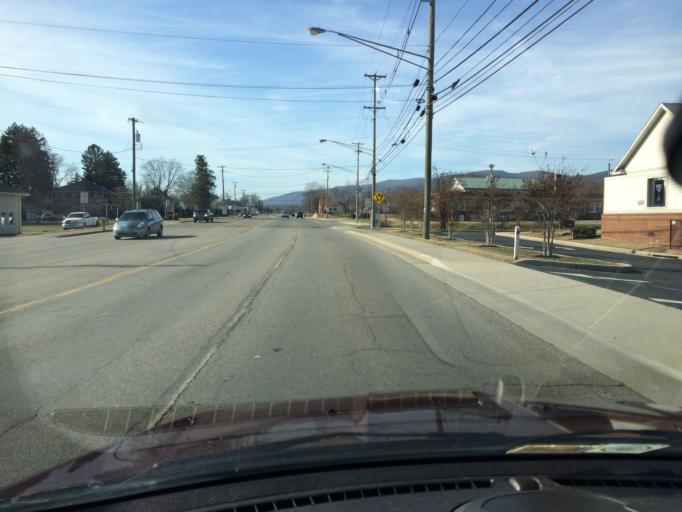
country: US
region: Virginia
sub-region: City of Salem
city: Salem
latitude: 37.2815
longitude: -80.1110
